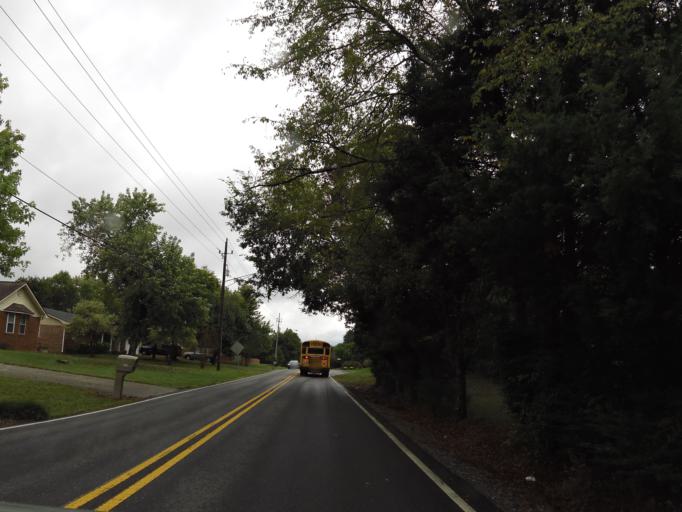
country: US
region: Tennessee
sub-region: Bradley County
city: Hopewell
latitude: 35.1999
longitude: -84.9071
